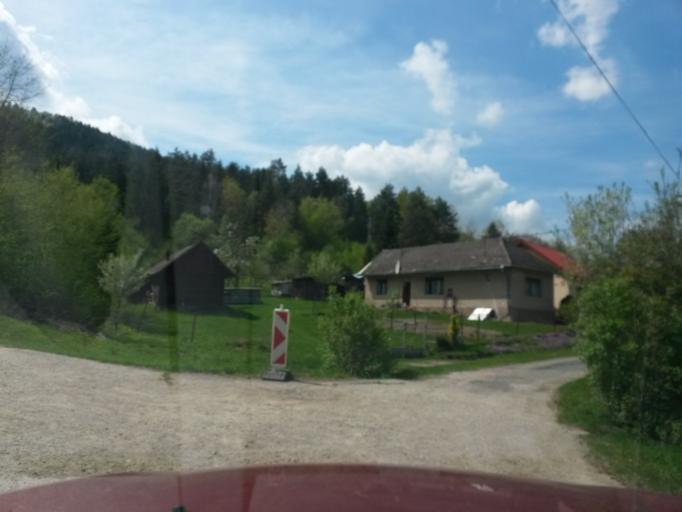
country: SK
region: Kosicky
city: Gelnica
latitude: 48.8162
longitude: 20.8859
